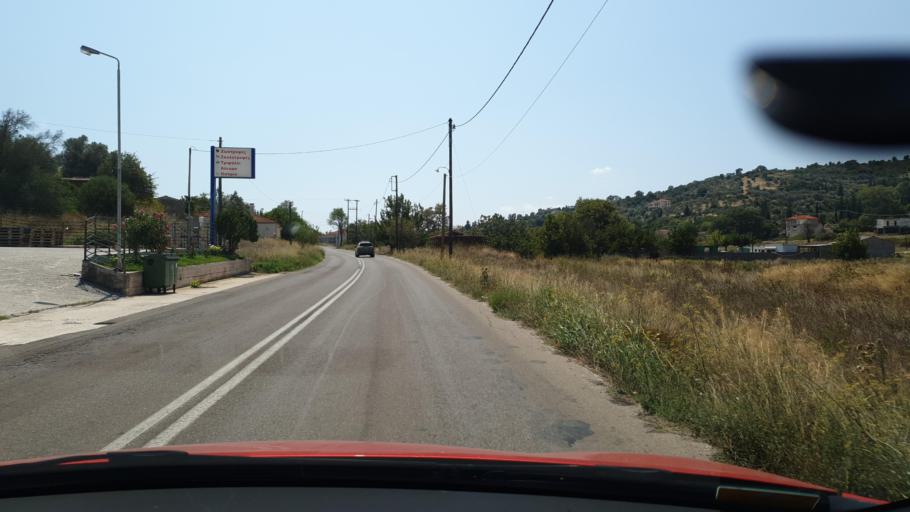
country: GR
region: Central Greece
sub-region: Nomos Evvoias
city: Oxilithos
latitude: 38.4837
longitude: 24.1180
